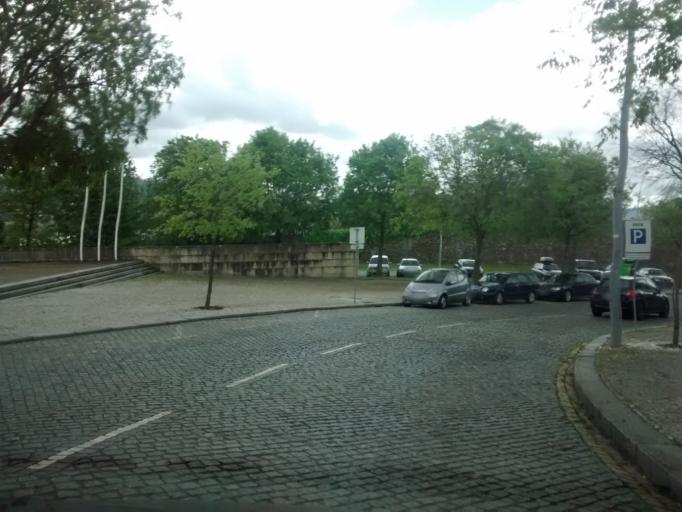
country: PT
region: Braga
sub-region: Braga
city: Braga
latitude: 41.5460
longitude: -8.4279
